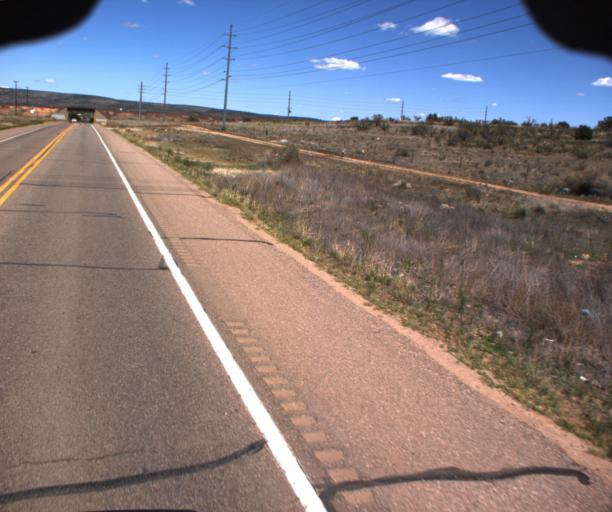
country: US
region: Arizona
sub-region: Yavapai County
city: Paulden
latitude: 34.8875
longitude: -112.4677
